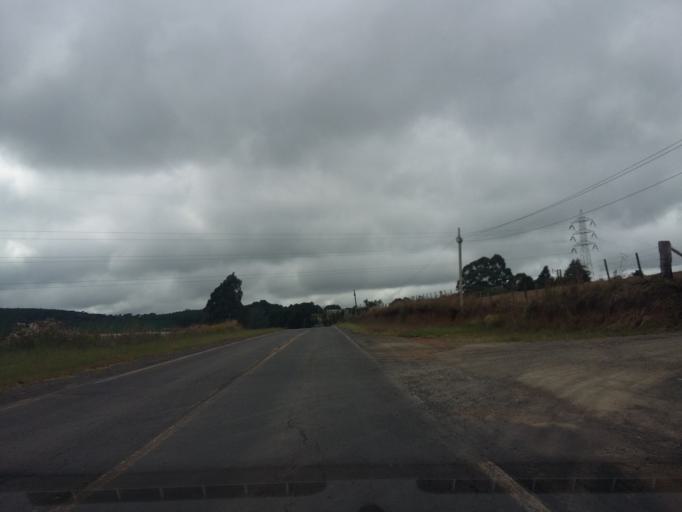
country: BR
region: Santa Catarina
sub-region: Lages
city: Lages
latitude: -27.8169
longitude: -50.2693
